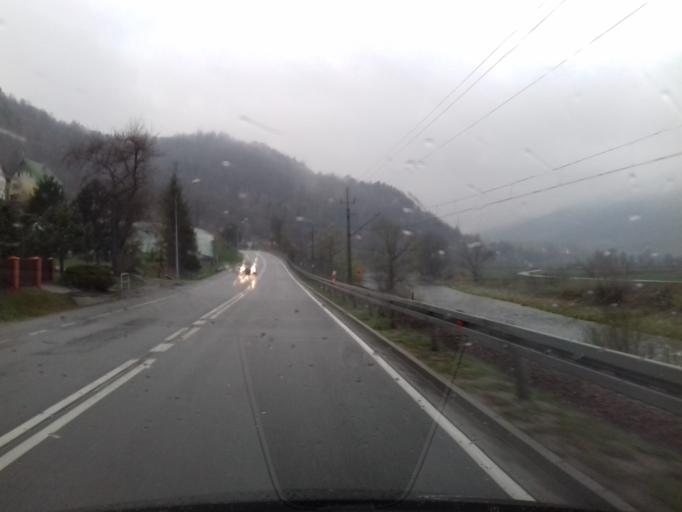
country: PL
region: Lesser Poland Voivodeship
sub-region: Powiat nowosadecki
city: Piwniczna-Zdroj
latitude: 49.4539
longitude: 20.6963
